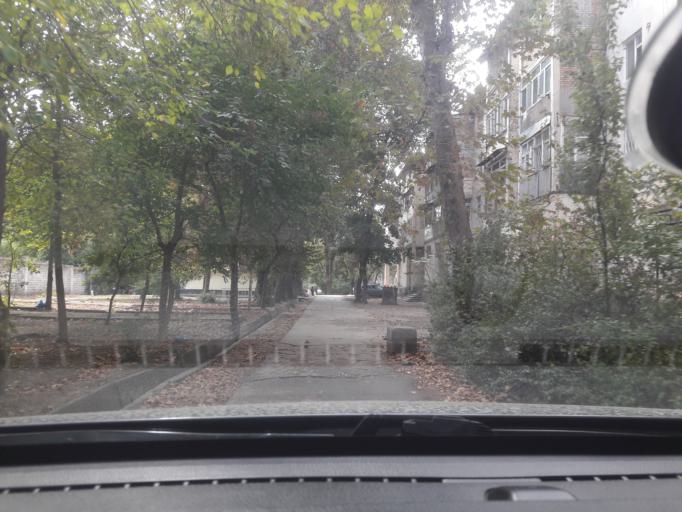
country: TJ
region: Dushanbe
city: Dushanbe
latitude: 38.5868
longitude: 68.7500
